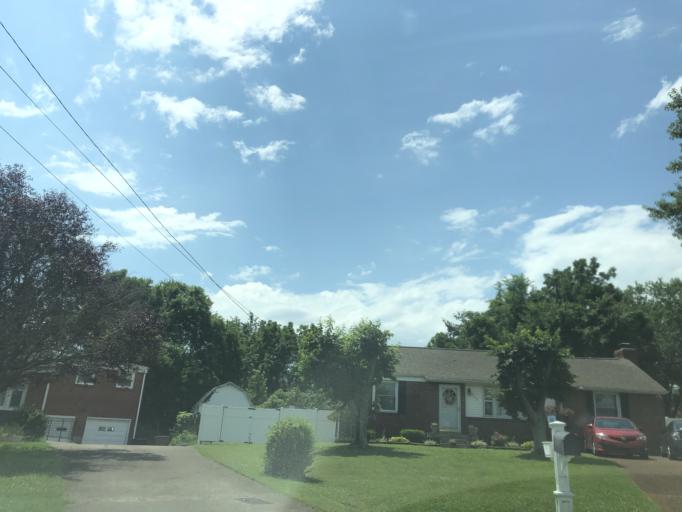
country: US
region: Tennessee
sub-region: Davidson County
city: Lakewood
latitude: 36.1593
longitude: -86.6497
